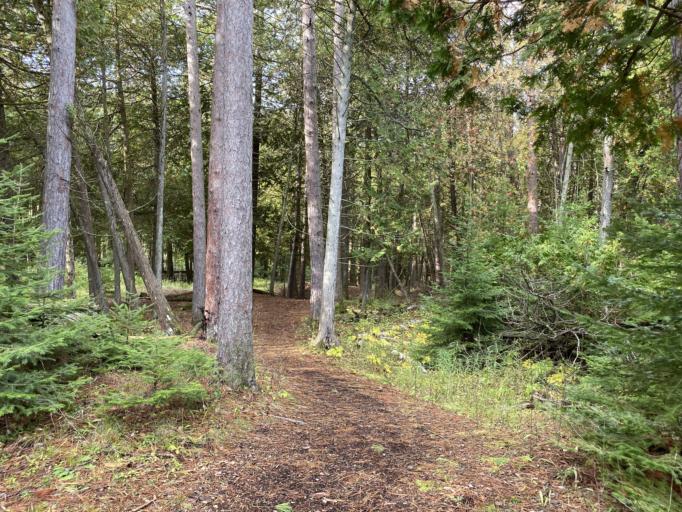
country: US
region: Michigan
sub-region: Mackinac County
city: Saint Ignace
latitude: 45.7515
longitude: -84.8805
